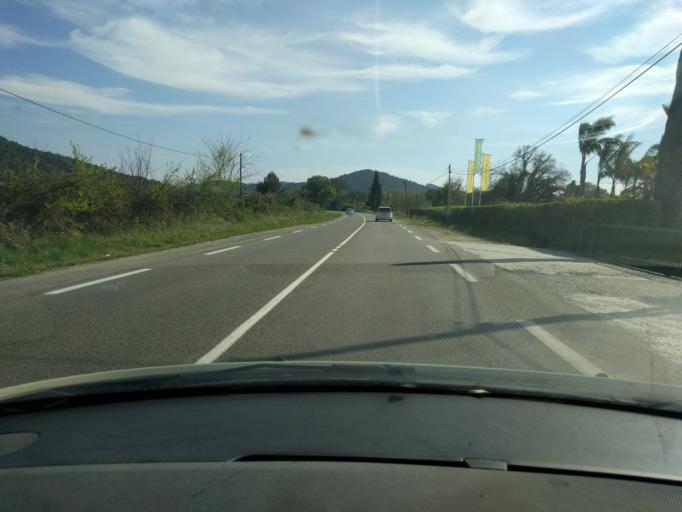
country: FR
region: Provence-Alpes-Cote d'Azur
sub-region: Departement du Var
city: Pierrefeu-du-Var
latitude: 43.1793
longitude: 6.1181
